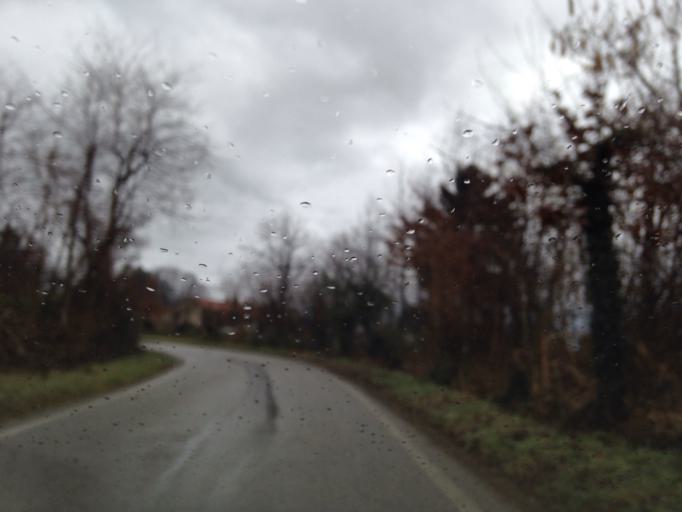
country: IT
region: Piedmont
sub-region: Provincia di Vercelli
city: Moncrivello
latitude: 45.3217
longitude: 7.9944
